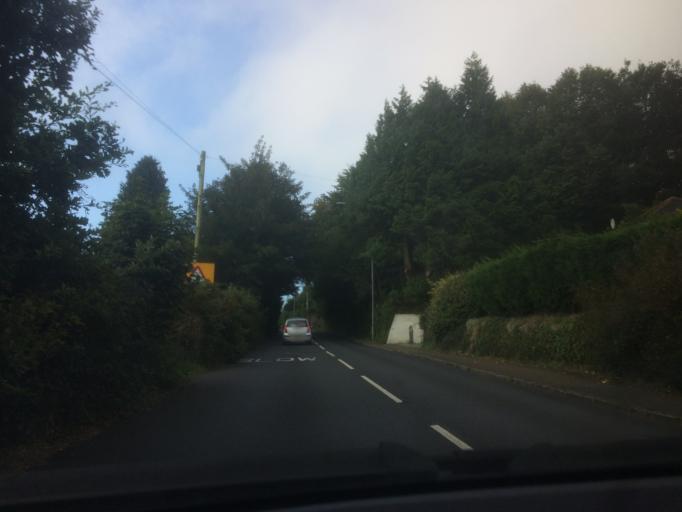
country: GB
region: England
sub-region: Cornwall
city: Gunnislake
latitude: 50.5181
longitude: -4.2186
